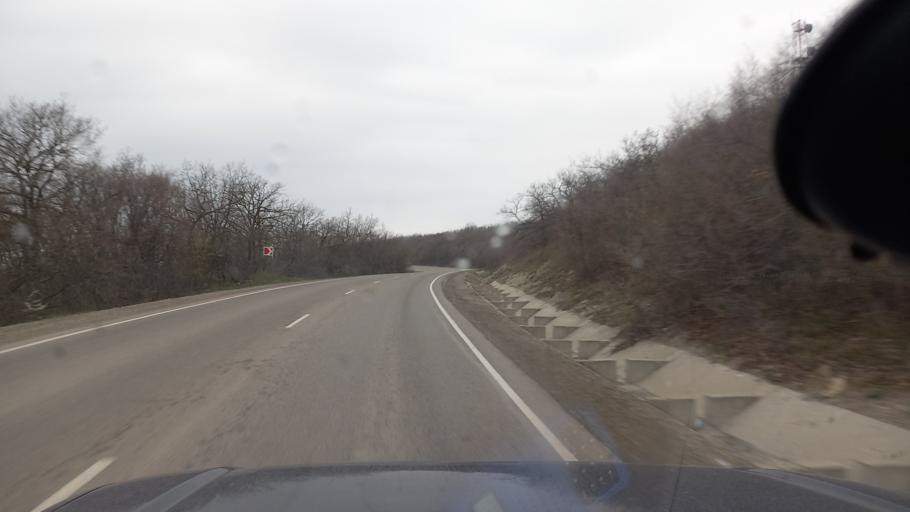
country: RU
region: Krasnodarskiy
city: Sukko
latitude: 44.8401
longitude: 37.4171
